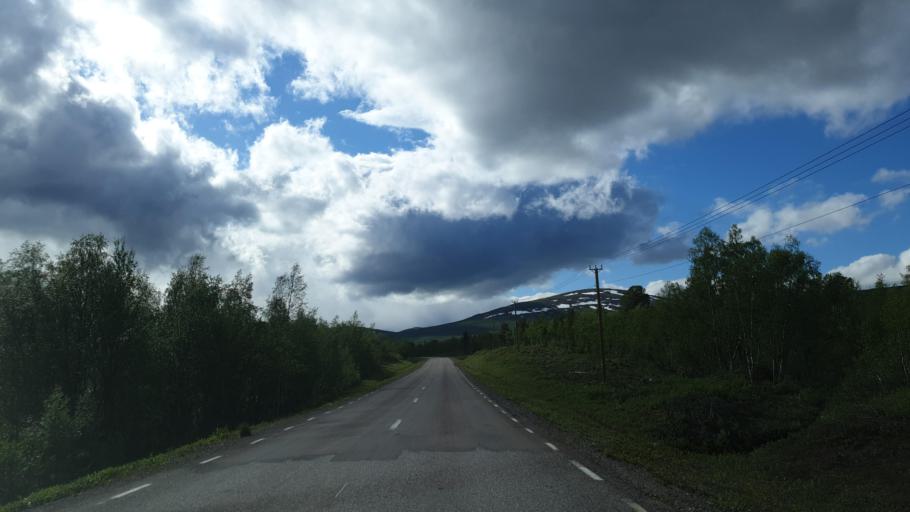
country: SE
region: Norrbotten
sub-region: Kiruna Kommun
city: Kiruna
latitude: 67.8704
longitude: 19.2507
